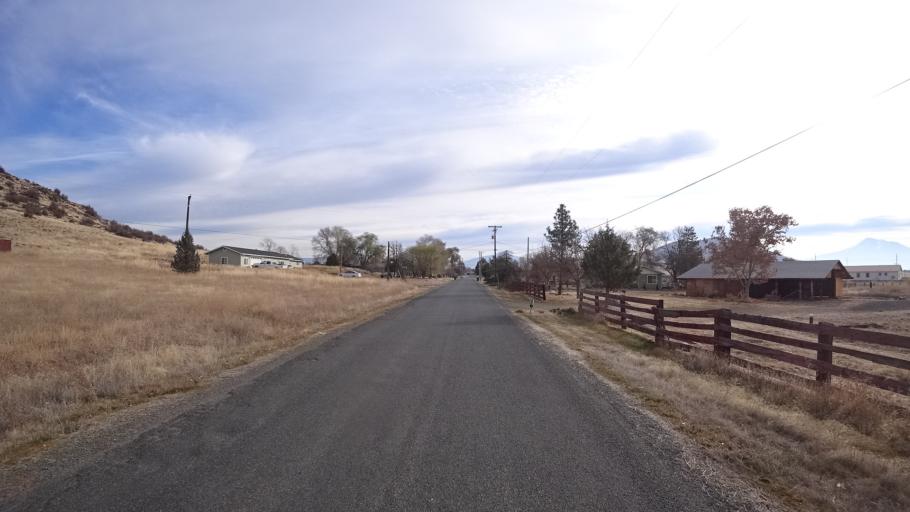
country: US
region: California
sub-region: Siskiyou County
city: Montague
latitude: 41.7264
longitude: -122.5401
